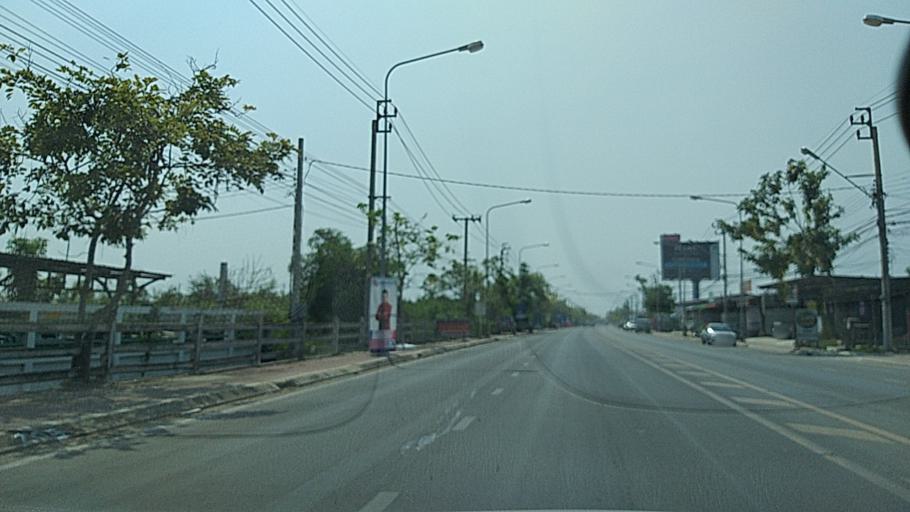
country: TH
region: Nonthaburi
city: Sai Noi
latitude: 13.9098
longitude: 100.3311
